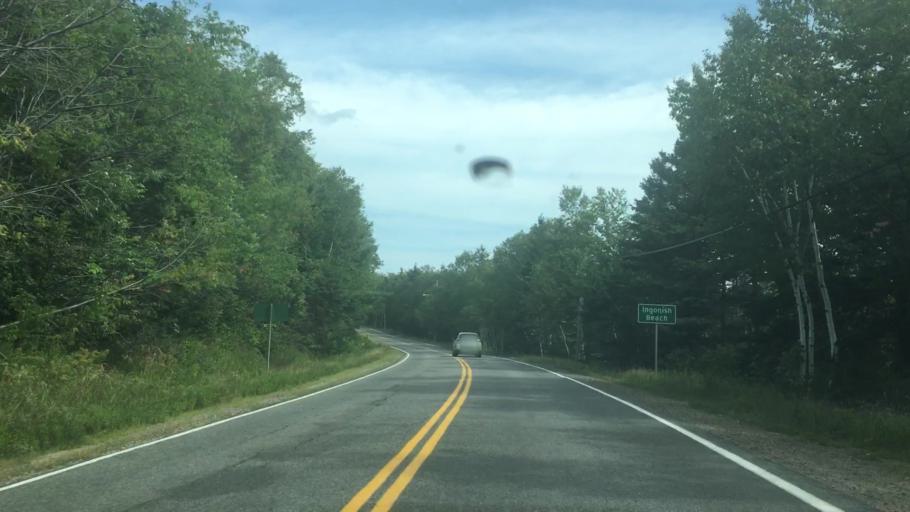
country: CA
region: Nova Scotia
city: Sydney Mines
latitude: 46.6355
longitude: -60.4187
